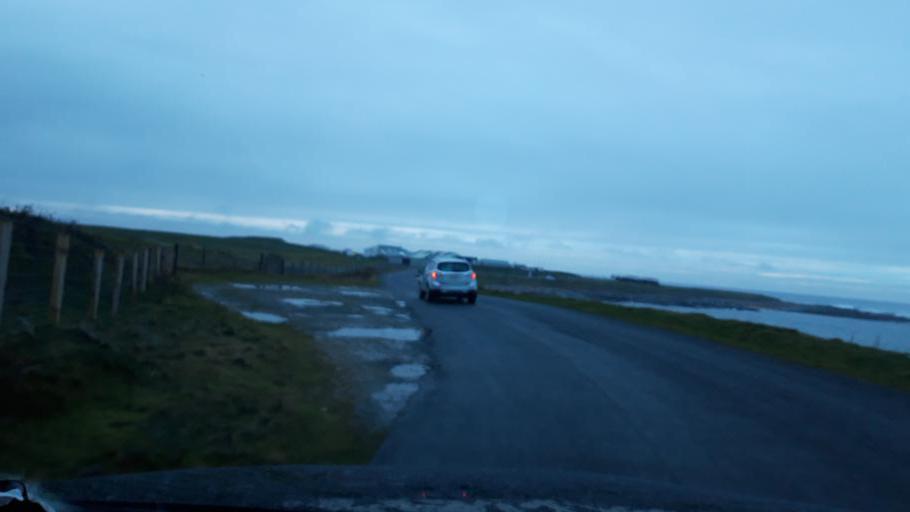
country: IE
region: Ulster
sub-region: County Donegal
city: Ramelton
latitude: 55.2614
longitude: -7.6844
